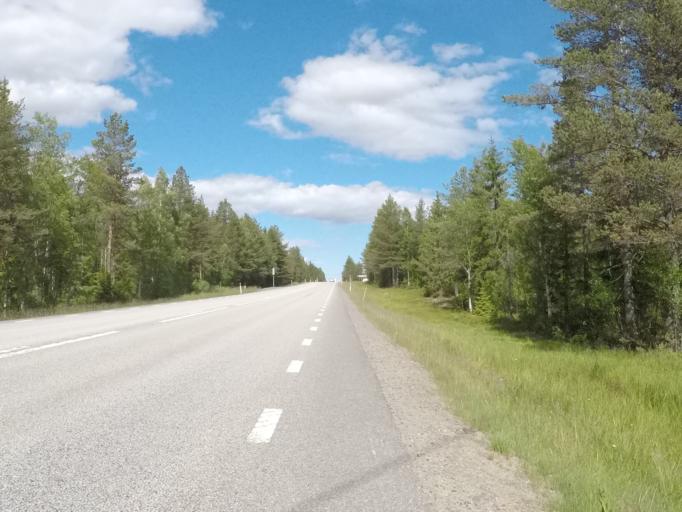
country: SE
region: Vaesterbotten
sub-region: Robertsfors Kommun
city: Robertsfors
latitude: 64.1897
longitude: 20.9986
